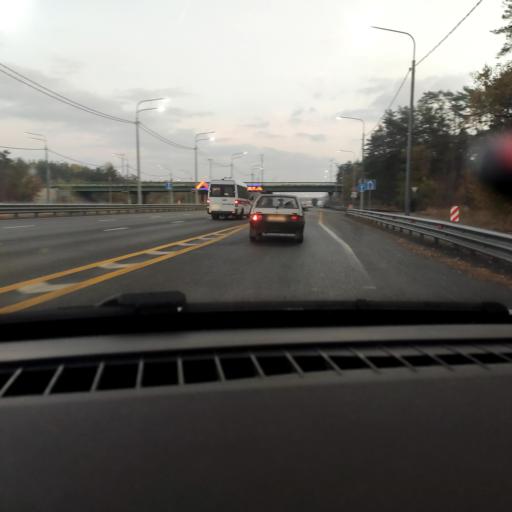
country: RU
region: Voronezj
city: Podgornoye
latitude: 51.7338
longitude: 39.1805
